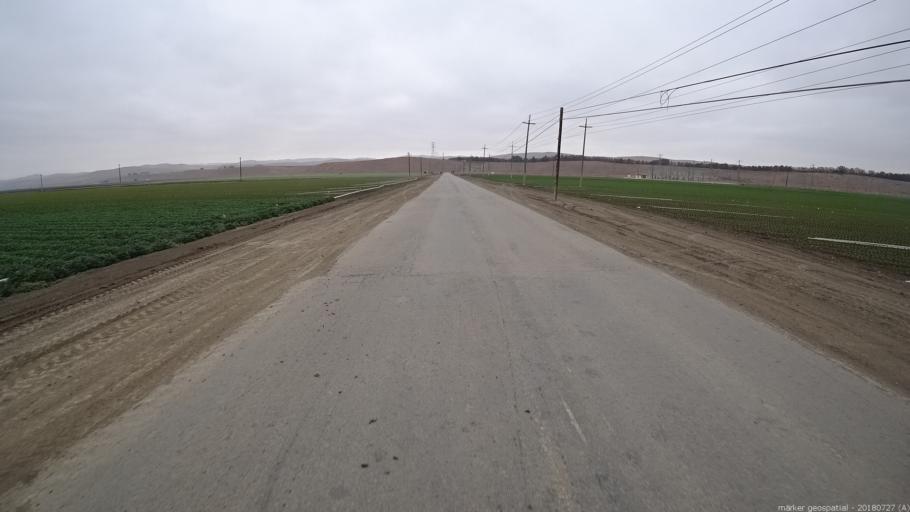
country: US
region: California
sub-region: Monterey County
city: King City
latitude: 36.2645
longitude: -121.1507
